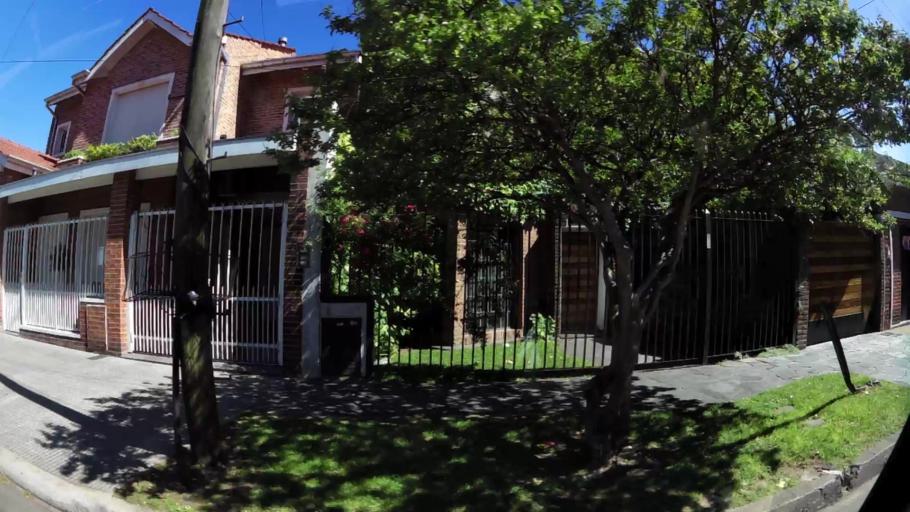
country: AR
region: Buenos Aires
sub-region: Partido de Vicente Lopez
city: Olivos
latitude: -34.5263
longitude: -58.5027
